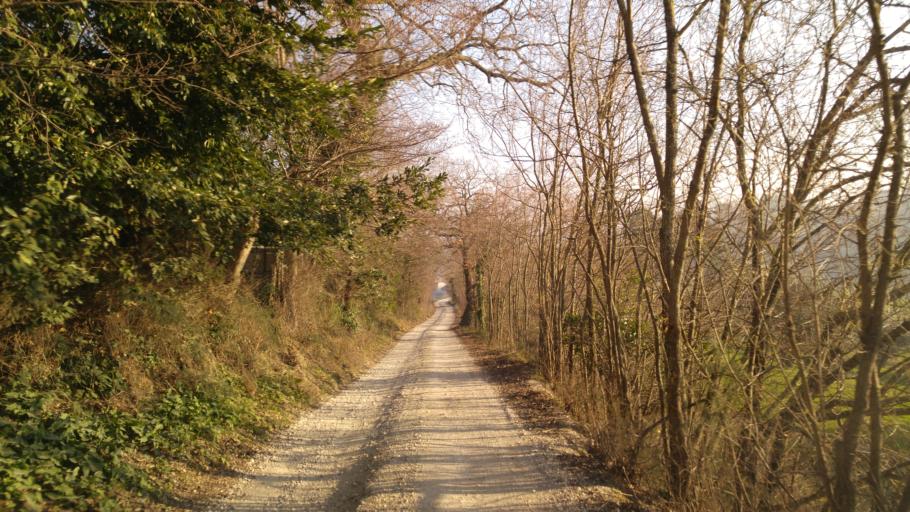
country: IT
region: The Marches
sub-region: Provincia di Pesaro e Urbino
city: Fenile
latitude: 43.8505
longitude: 12.9643
